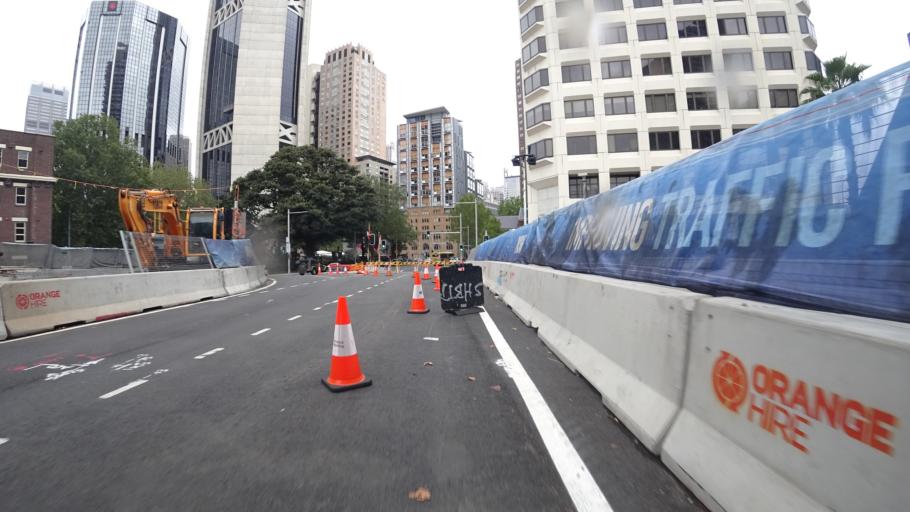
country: AU
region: New South Wales
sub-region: City of Sydney
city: Sydney
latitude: -33.8632
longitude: 151.2050
